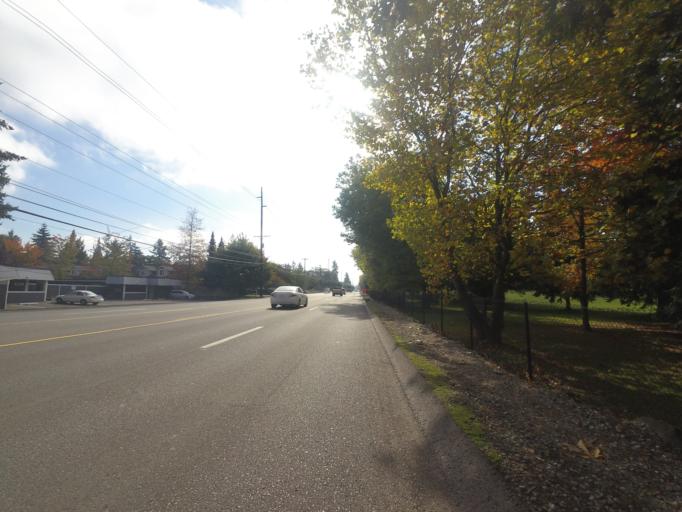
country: US
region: Washington
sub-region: Pierce County
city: Lakewood
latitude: 47.1956
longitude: -122.5089
